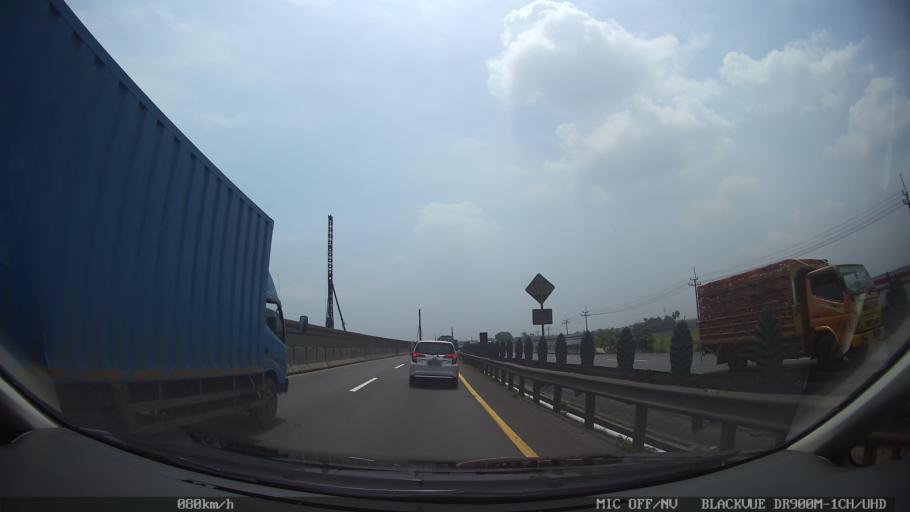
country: ID
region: West Java
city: Kresek
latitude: -6.1489
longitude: 106.2996
